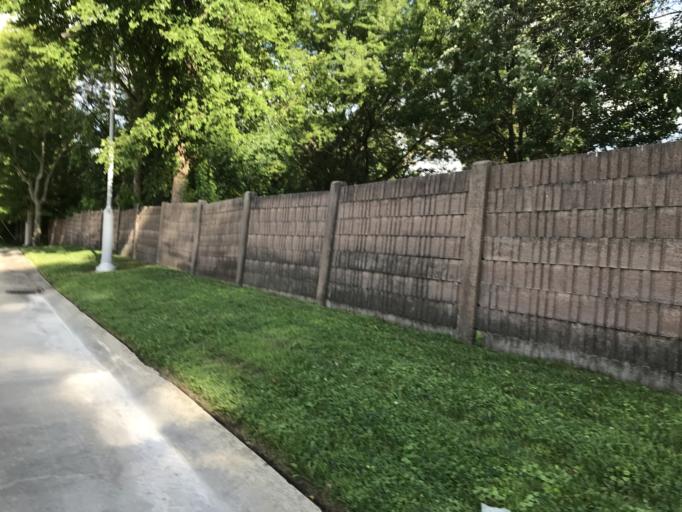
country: US
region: Michigan
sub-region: Oakland County
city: Farmington
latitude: 42.4692
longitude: -83.3529
